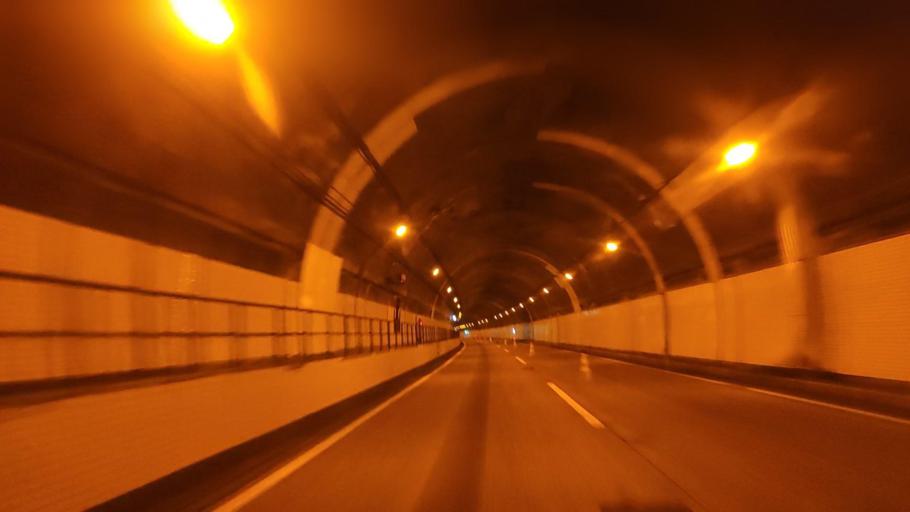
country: JP
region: Niigata
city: Itoigawa
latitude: 36.9892
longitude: 137.6919
